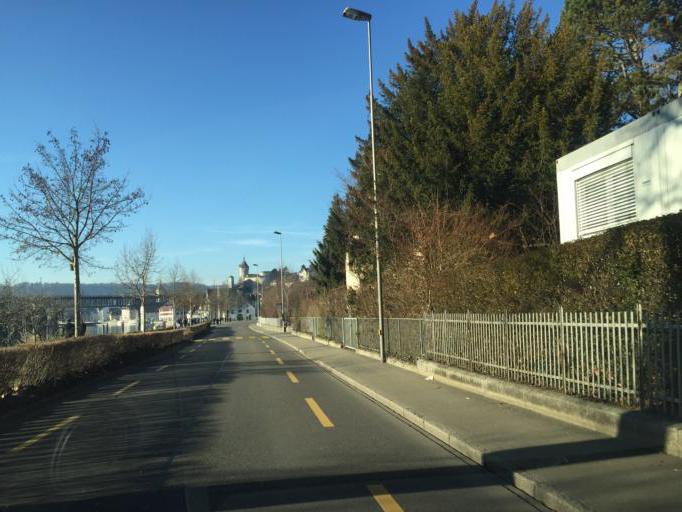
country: CH
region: Zurich
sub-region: Bezirk Andelfingen
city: Feuerthalen
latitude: 47.6936
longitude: 8.6489
